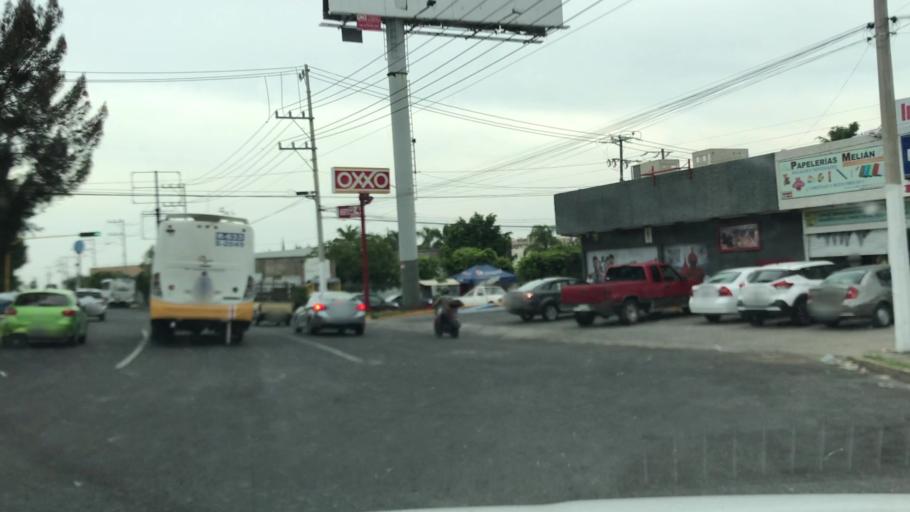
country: MX
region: Jalisco
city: Nuevo Mexico
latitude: 20.7489
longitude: -103.4183
